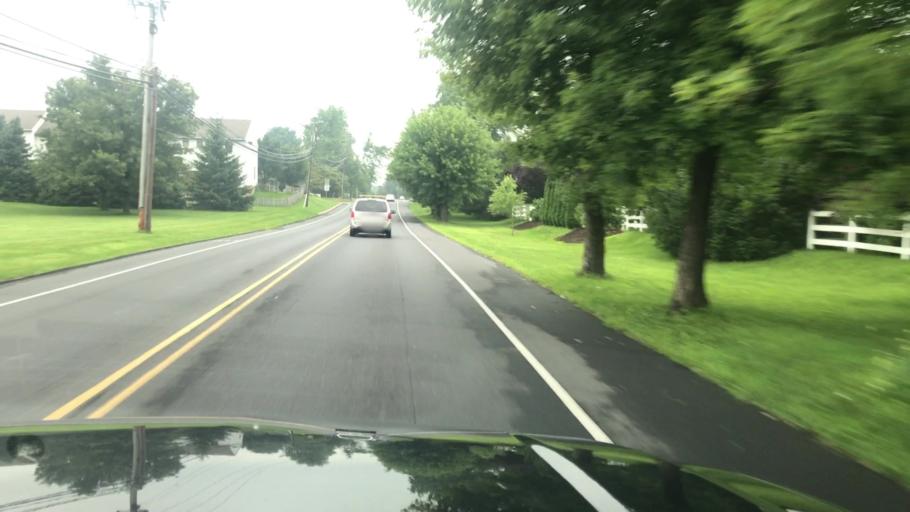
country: US
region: Pennsylvania
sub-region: Cumberland County
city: Enola
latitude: 40.2760
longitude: -76.9702
